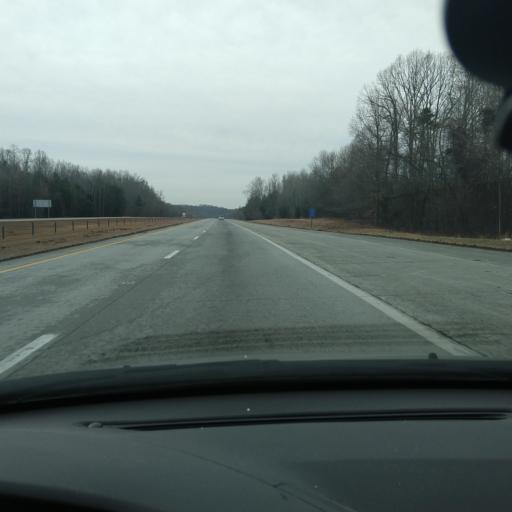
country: US
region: North Carolina
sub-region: Davidson County
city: Welcome
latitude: 35.8648
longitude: -80.2685
